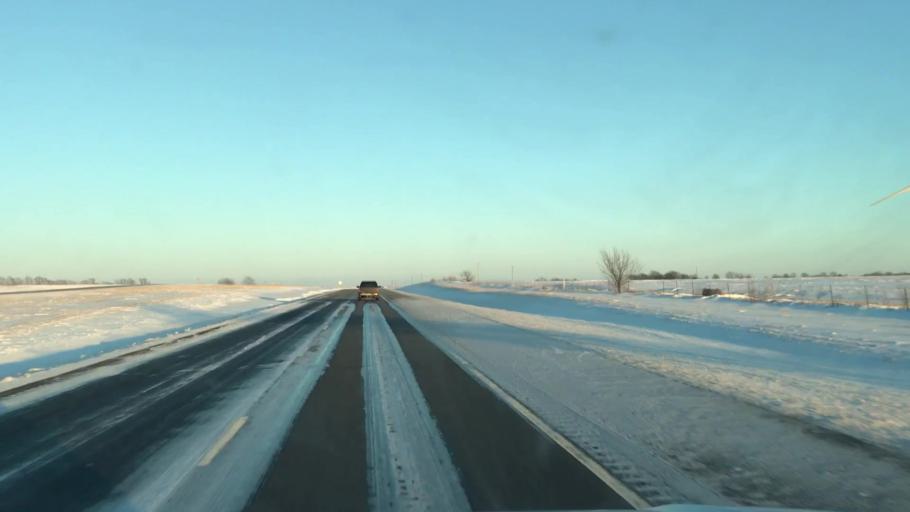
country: US
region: Missouri
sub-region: DeKalb County
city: Maysville
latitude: 39.7615
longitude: -94.3792
